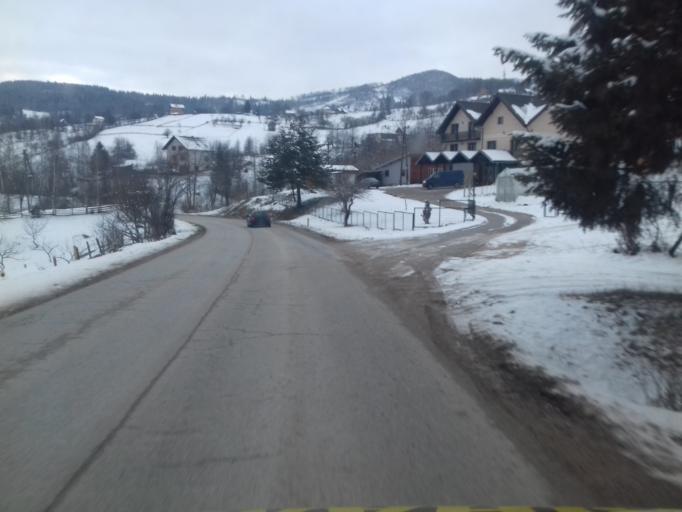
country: BA
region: Republika Srpska
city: Pale
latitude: 43.8725
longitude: 18.5603
